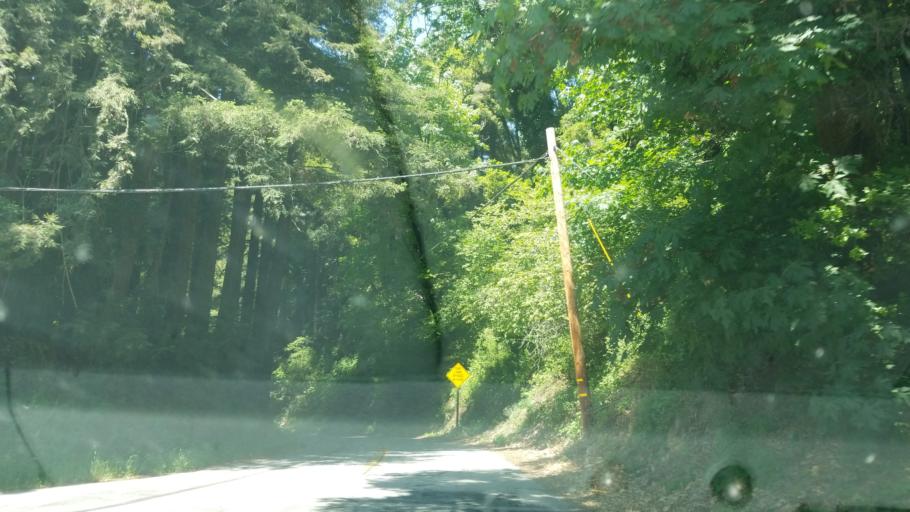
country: US
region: California
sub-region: Santa Cruz County
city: Interlaken
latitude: 37.0009
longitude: -121.7396
